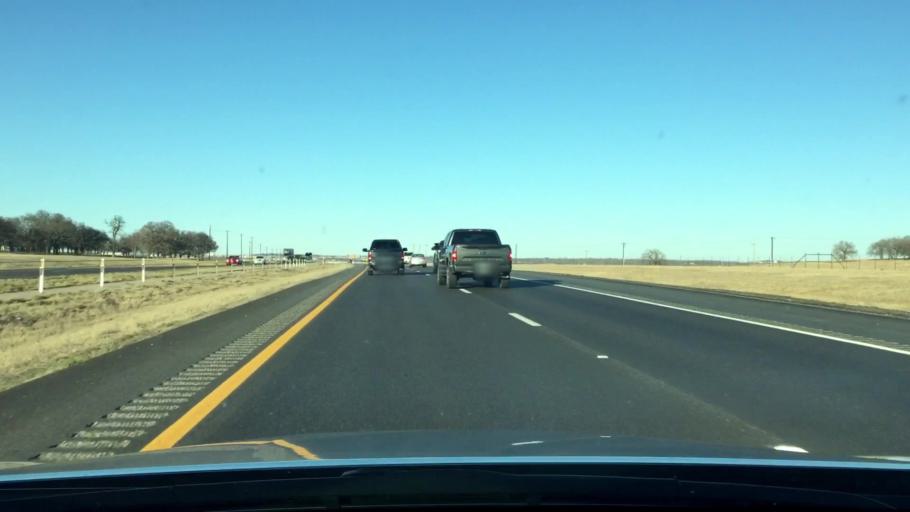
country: US
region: Texas
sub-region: Denton County
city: Argyle
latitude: 33.1459
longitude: -97.1969
